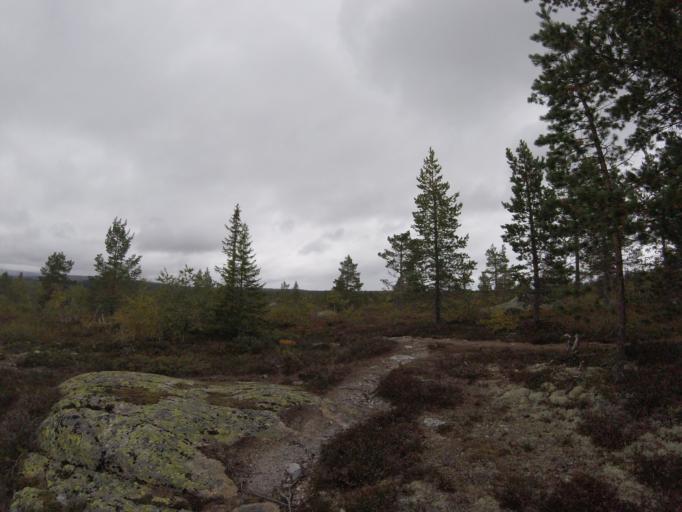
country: NO
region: Buskerud
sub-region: Flesberg
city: Lampeland
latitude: 59.7576
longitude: 9.4021
